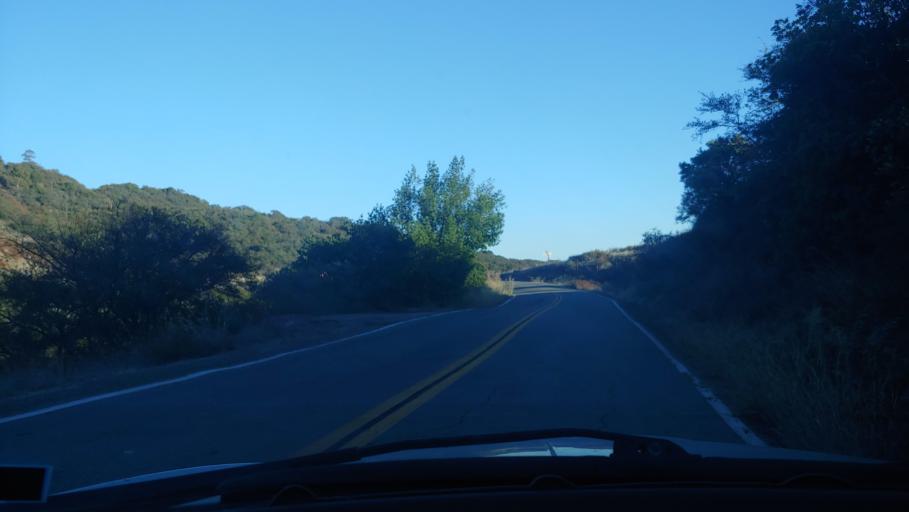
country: US
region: California
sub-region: Santa Barbara County
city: Goleta
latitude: 34.5142
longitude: -119.7979
